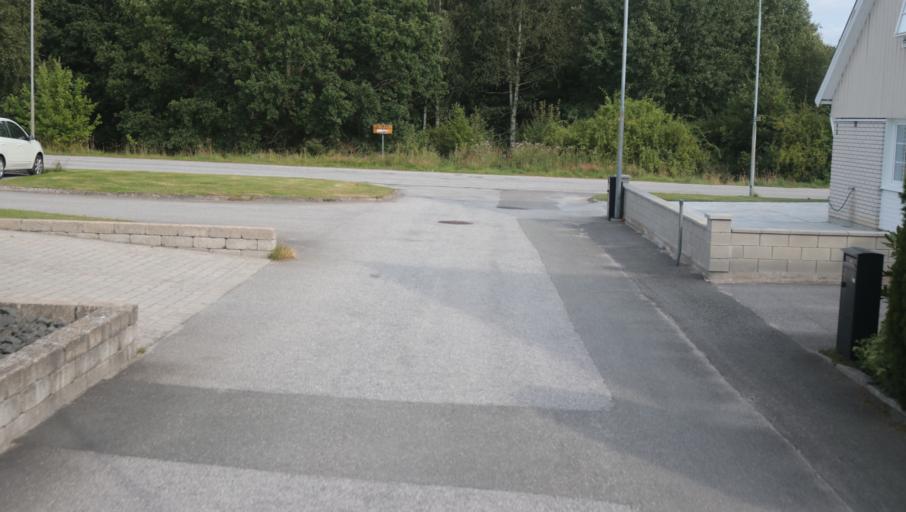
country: SE
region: Blekinge
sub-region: Karlshamns Kommun
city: Karlshamn
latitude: 56.2081
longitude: 14.8503
